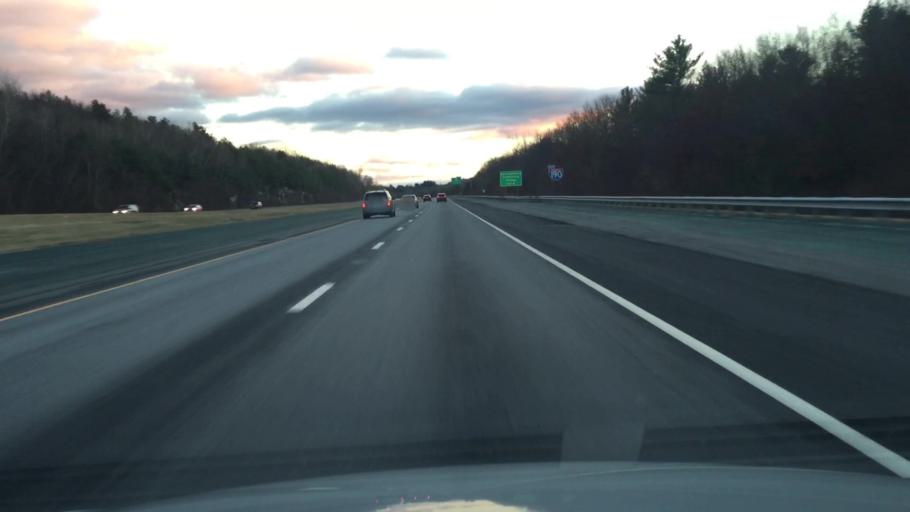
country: US
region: Massachusetts
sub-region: Worcester County
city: West Boylston
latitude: 42.3566
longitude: -71.8127
